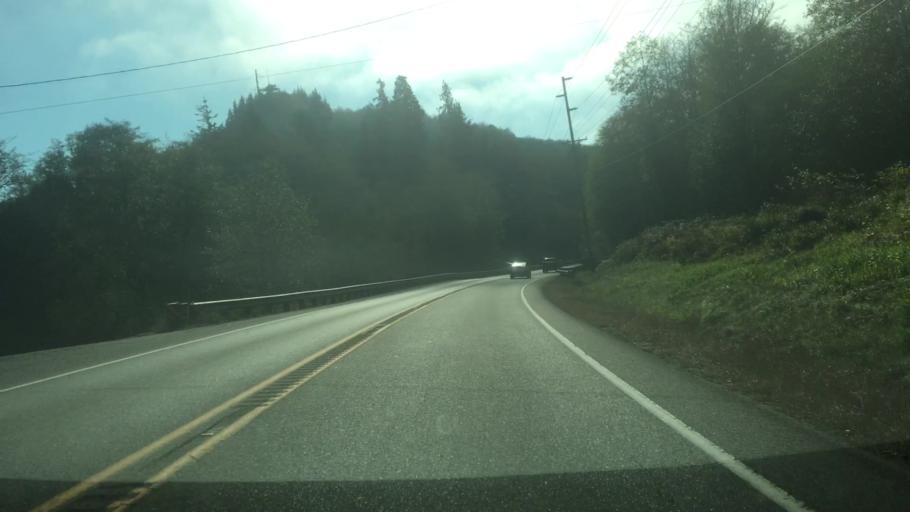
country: US
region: Washington
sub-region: Grays Harbor County
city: Montesano
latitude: 46.9514
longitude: -123.6123
